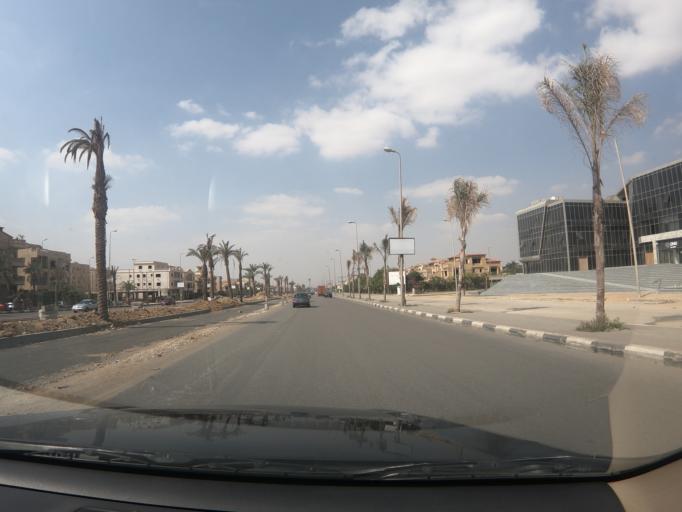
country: EG
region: Muhafazat al Qalyubiyah
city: Al Khankah
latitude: 30.0494
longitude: 31.4750
